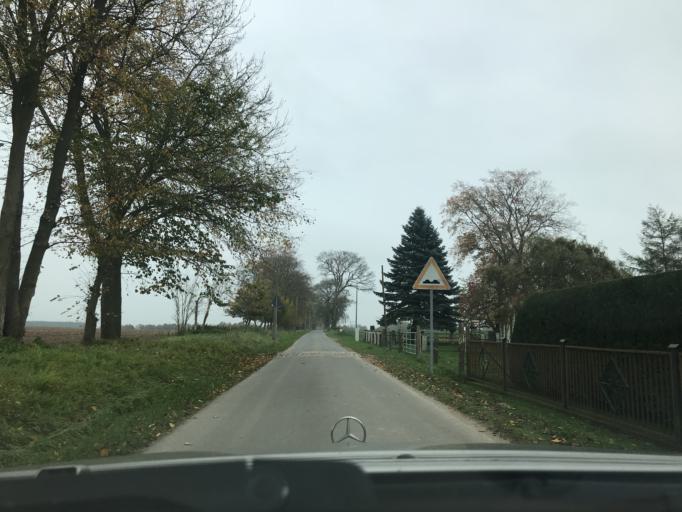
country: DE
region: Mecklenburg-Vorpommern
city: Kroslin
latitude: 54.1001
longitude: 13.7139
